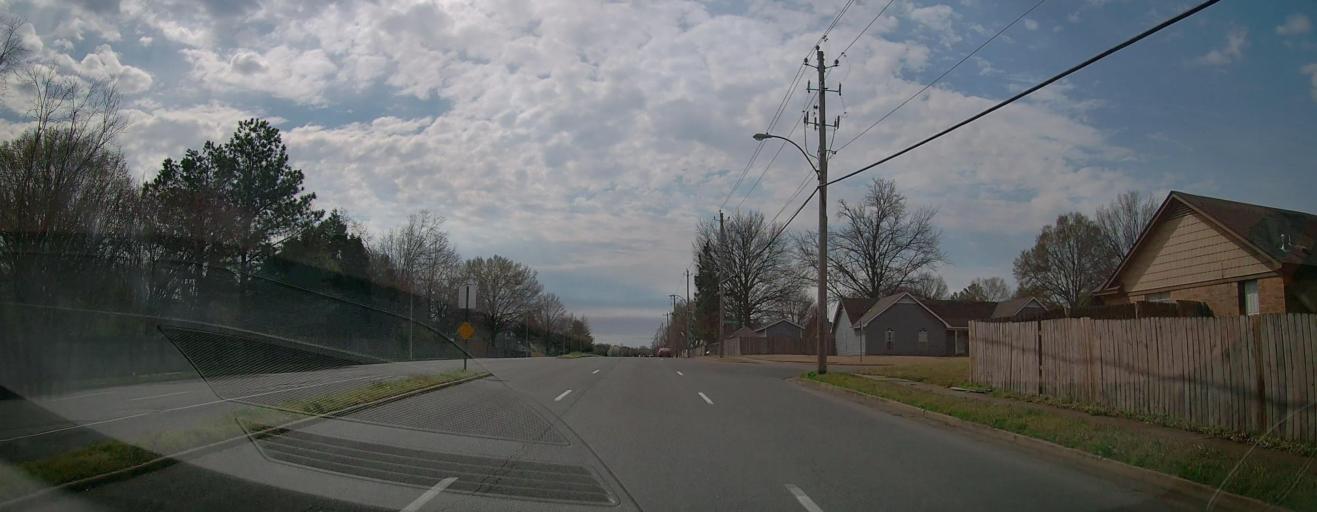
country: US
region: Tennessee
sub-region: Shelby County
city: Germantown
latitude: 35.0298
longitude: -89.8483
